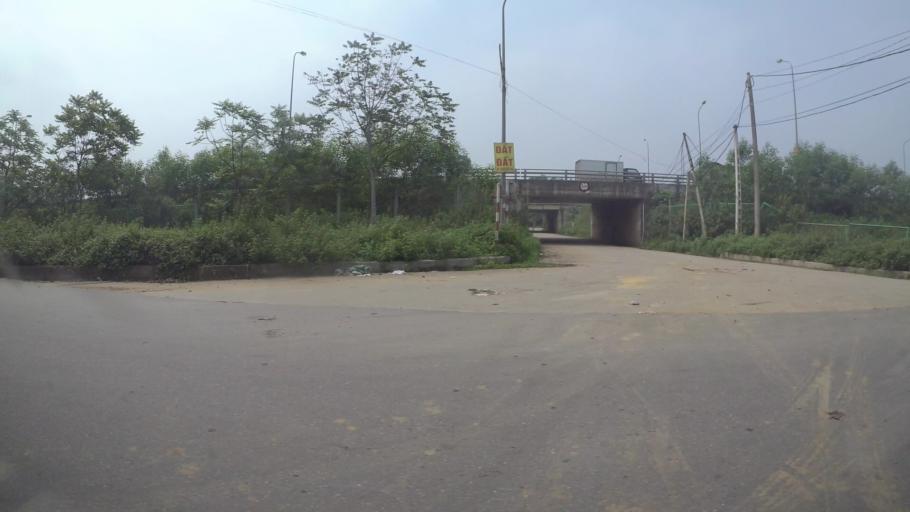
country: VN
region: Ha Noi
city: Lien Quan
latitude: 20.9903
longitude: 105.5594
